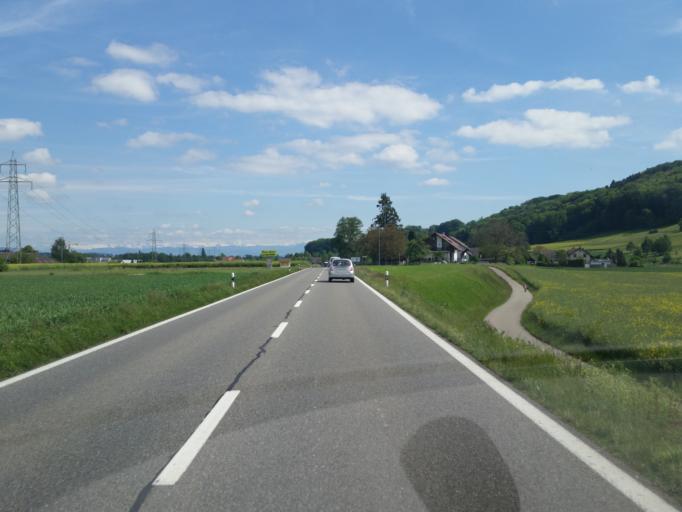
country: CH
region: Aargau
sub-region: Bezirk Bremgarten
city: Wohlen
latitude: 47.3364
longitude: 8.2774
